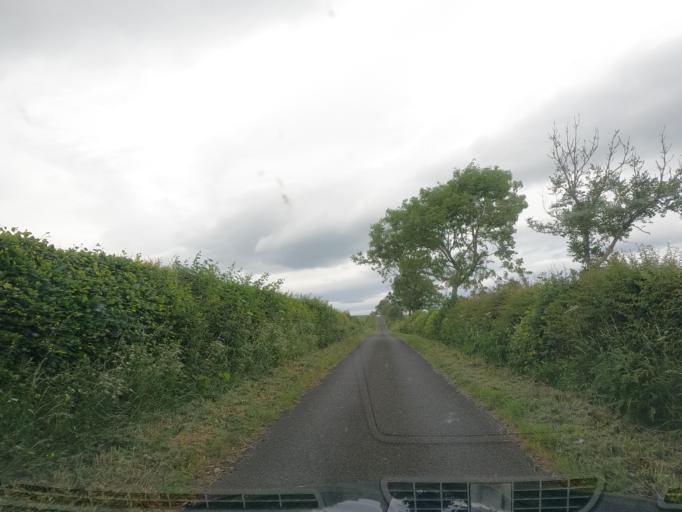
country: GB
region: England
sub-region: Northumberland
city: Lowick
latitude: 55.6088
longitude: -1.9682
